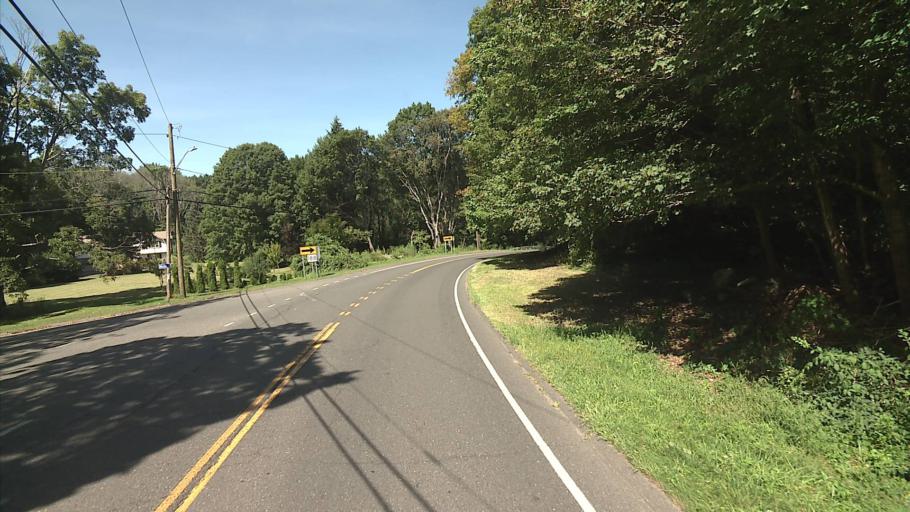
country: US
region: Connecticut
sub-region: New Haven County
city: Southbury
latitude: 41.4710
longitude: -73.1639
